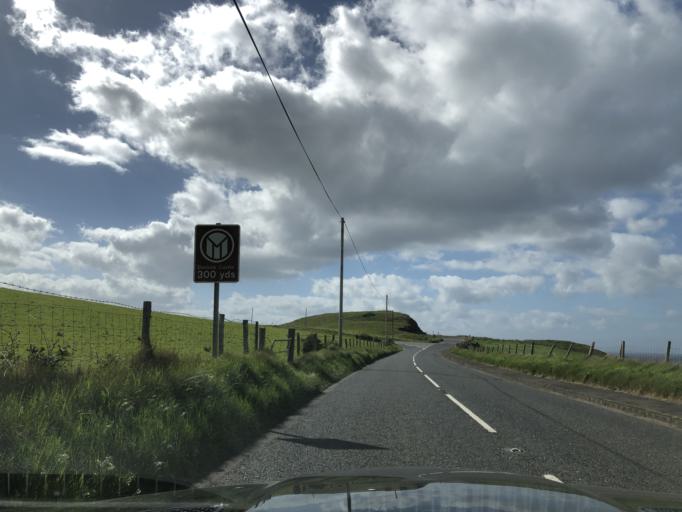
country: GB
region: Northern Ireland
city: Bushmills
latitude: 55.2122
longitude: -6.5705
